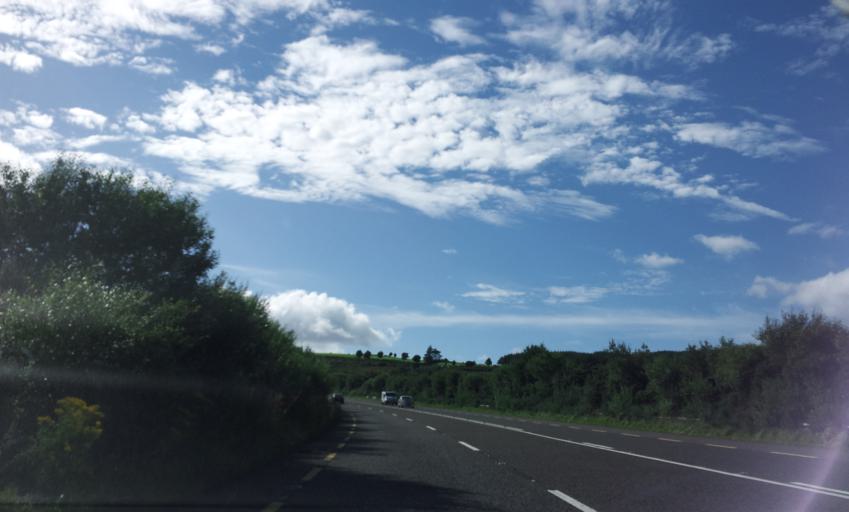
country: IE
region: Munster
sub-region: County Cork
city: Millstreet
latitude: 51.9622
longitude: -9.2070
